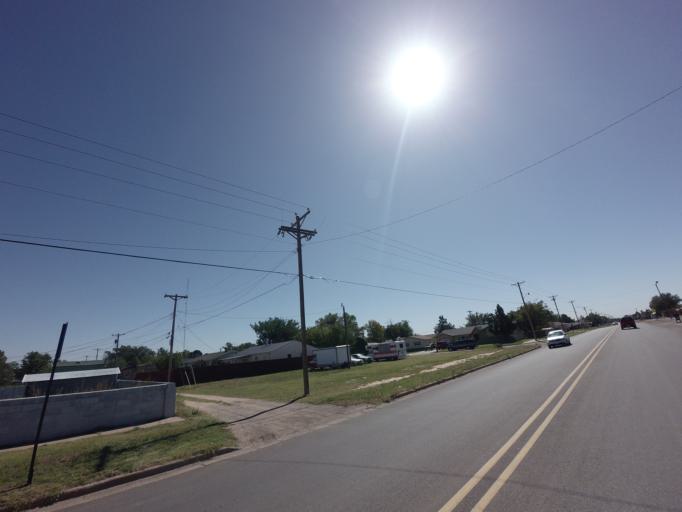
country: US
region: New Mexico
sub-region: Curry County
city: Clovis
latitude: 34.4180
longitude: -103.2142
